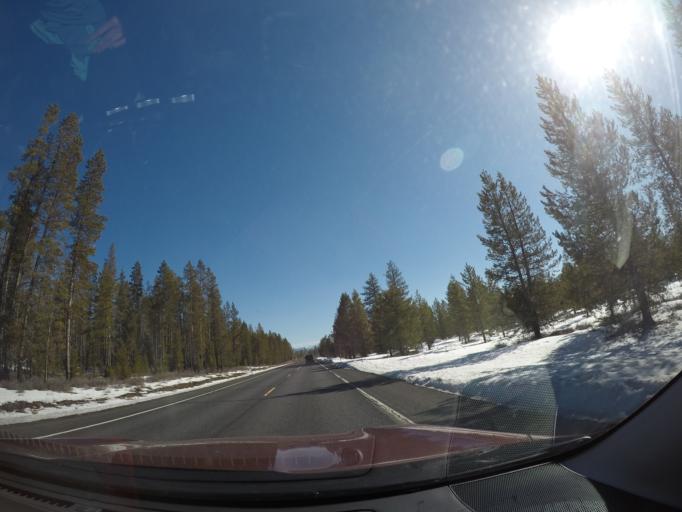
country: US
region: Oregon
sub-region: Deschutes County
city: Three Rivers
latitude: 43.8590
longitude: -121.5259
